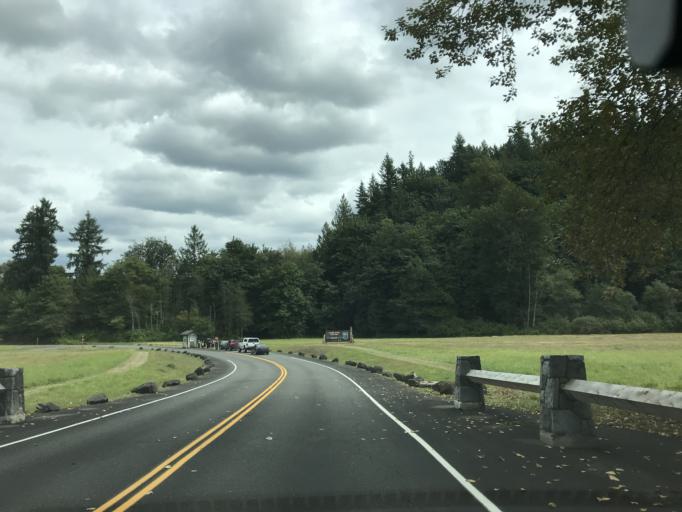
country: US
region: Washington
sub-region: King County
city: Black Diamond
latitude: 47.2786
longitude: -122.0379
